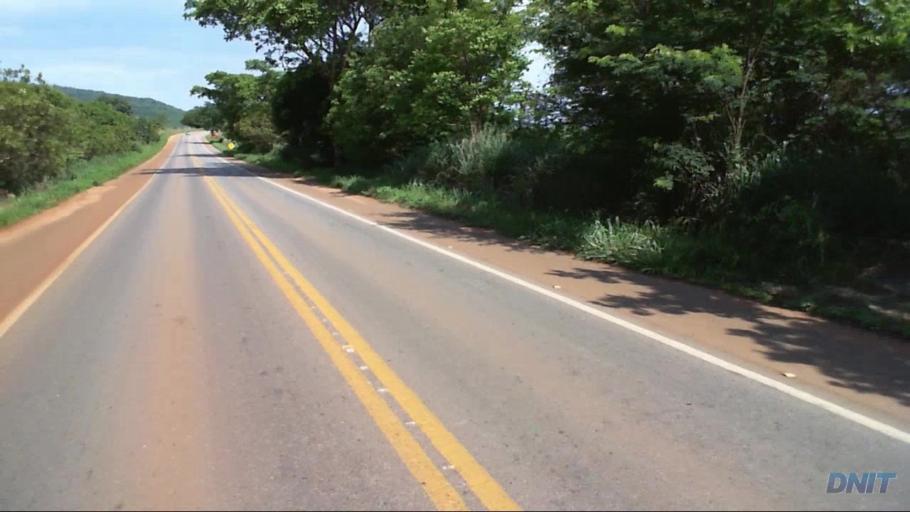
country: BR
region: Goias
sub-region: Barro Alto
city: Barro Alto
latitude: -15.0526
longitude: -48.8838
